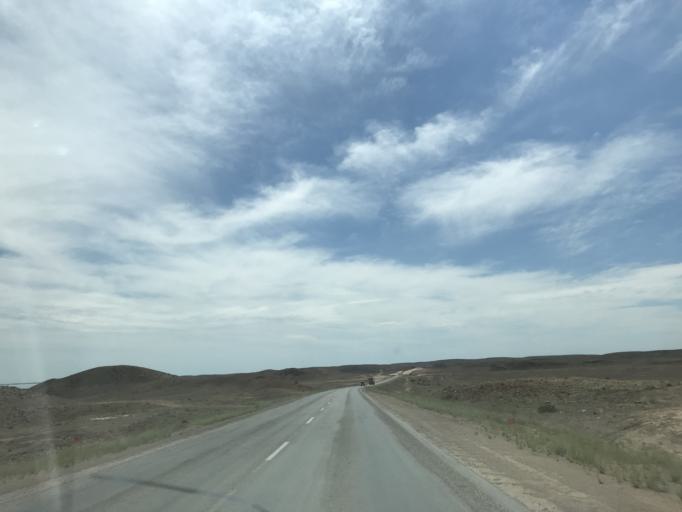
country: KZ
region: Almaty Oblysy
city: Ulken
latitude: 45.0739
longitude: 73.9867
